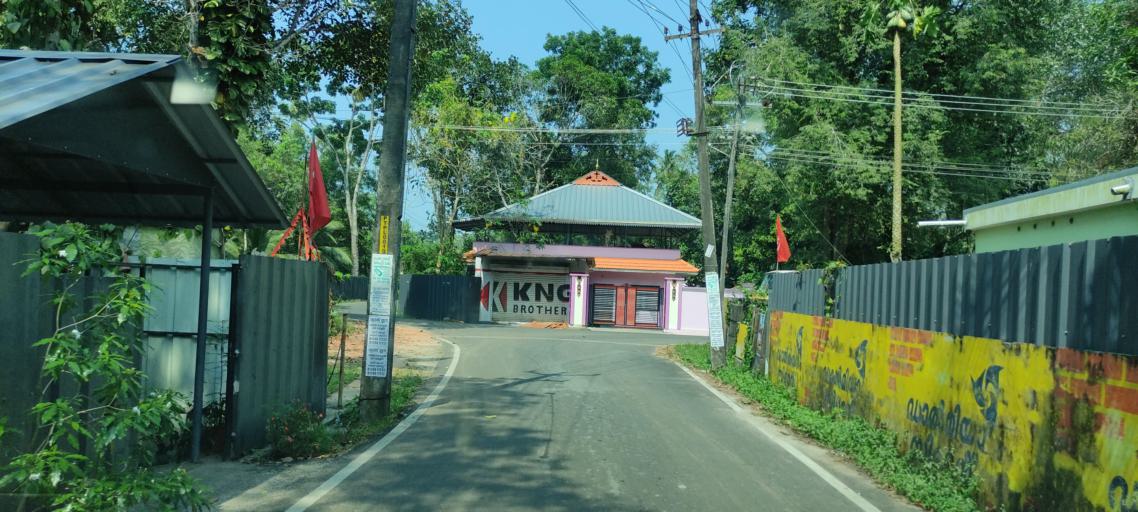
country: IN
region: Kerala
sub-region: Alappuzha
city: Alleppey
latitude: 9.5520
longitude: 76.3197
